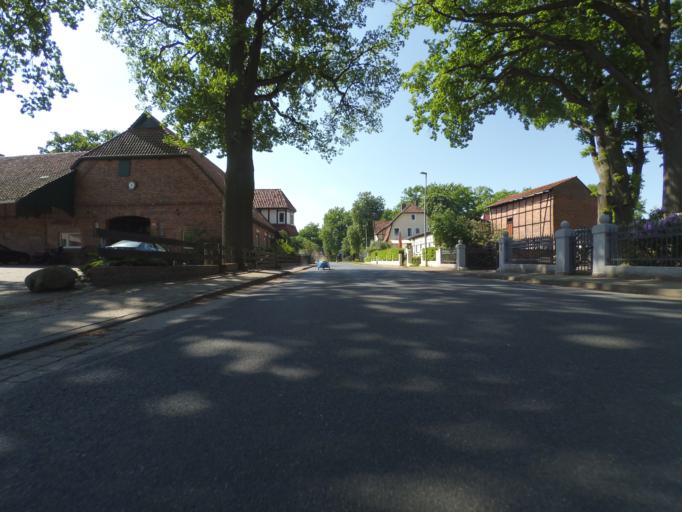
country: DE
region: Lower Saxony
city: Isernhagen Farster Bauerschaft
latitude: 52.4659
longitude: 9.8927
